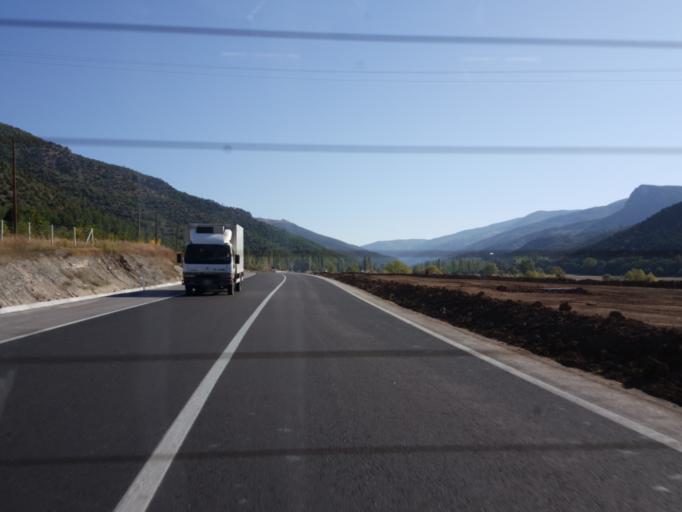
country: TR
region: Tokat
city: Turhal
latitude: 40.4707
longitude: 36.1286
